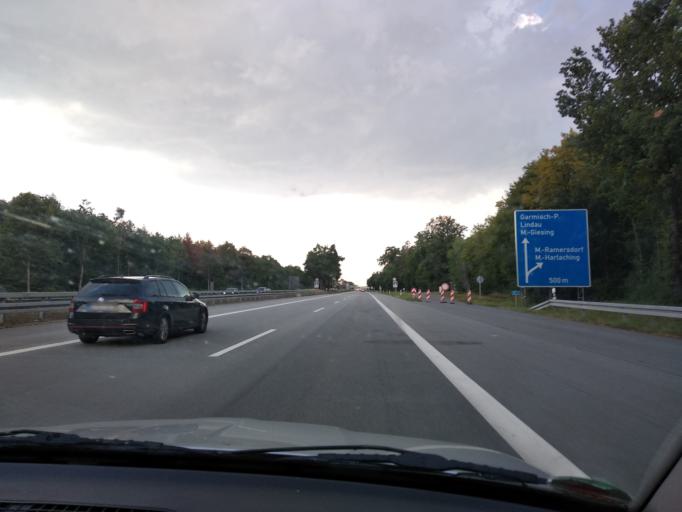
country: DE
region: Bavaria
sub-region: Upper Bavaria
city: Unterhaching
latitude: 48.0899
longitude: 11.5914
